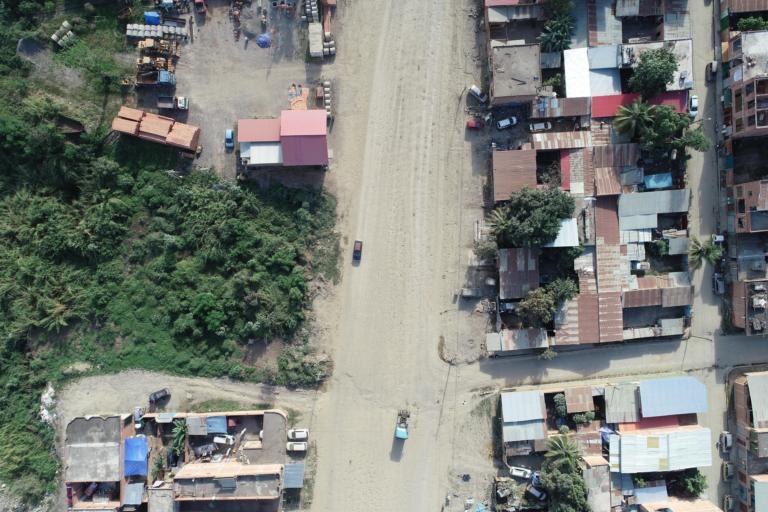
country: BO
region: La Paz
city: Coroico
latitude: -15.8372
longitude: -67.5619
